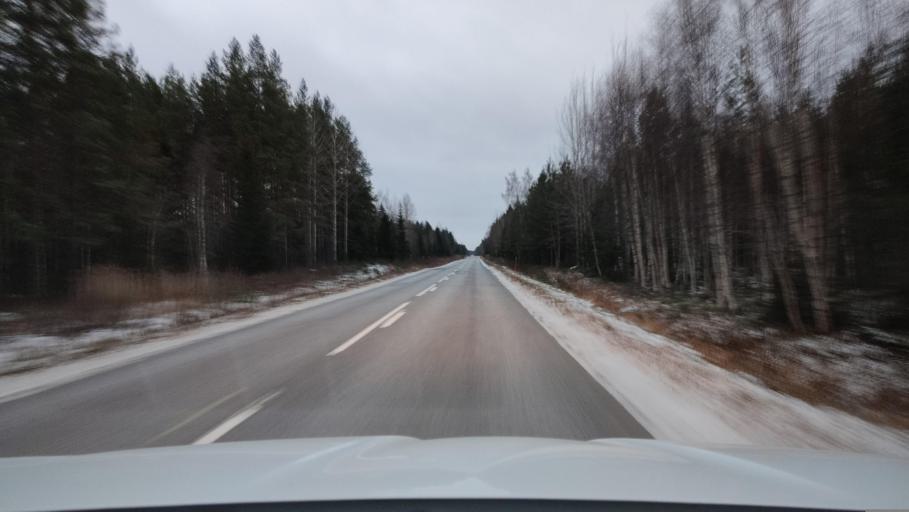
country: FI
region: Ostrobothnia
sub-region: Vaasa
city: Replot
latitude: 63.2629
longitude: 21.3598
